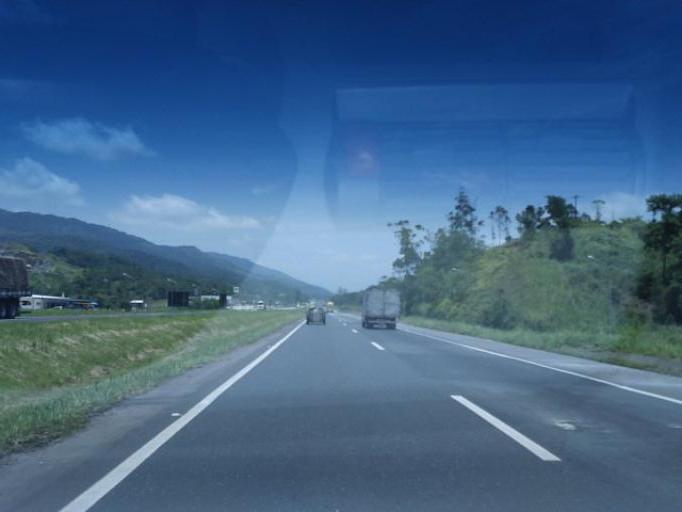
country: BR
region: Sao Paulo
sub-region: Miracatu
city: Miracatu
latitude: -24.2711
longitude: -47.4025
